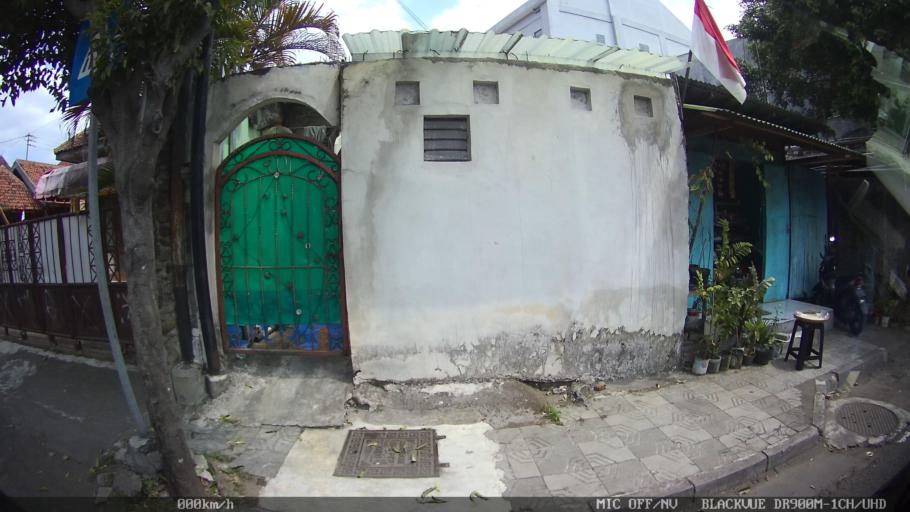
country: ID
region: Daerah Istimewa Yogyakarta
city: Yogyakarta
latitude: -7.7781
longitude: 110.3618
